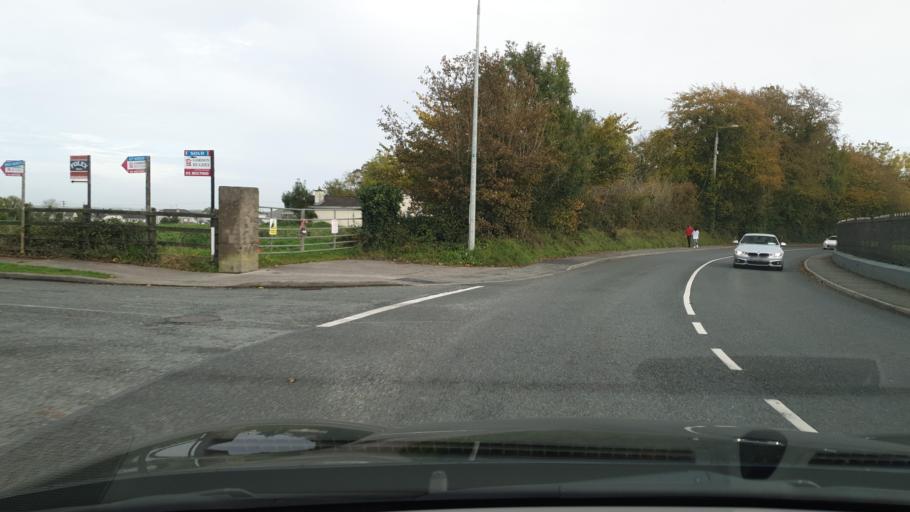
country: IE
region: Leinster
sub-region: An Mhi
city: Ratoath
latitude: 53.5068
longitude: -6.4584
